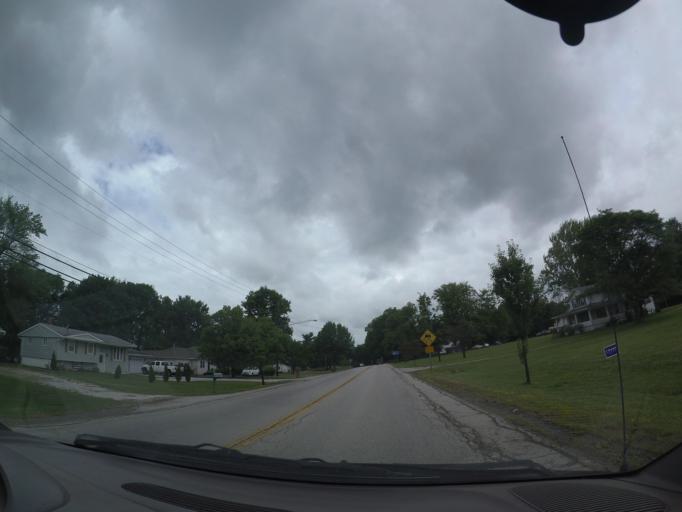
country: US
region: Ohio
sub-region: Ashtabula County
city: Geneva
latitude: 41.7863
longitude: -80.9467
